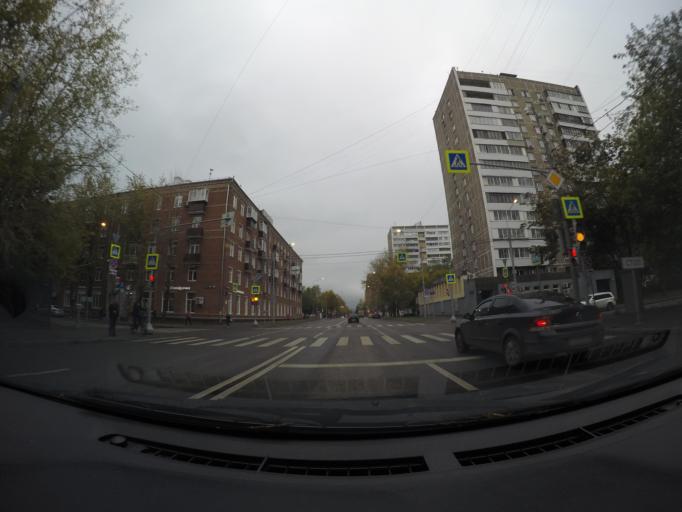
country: RU
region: Moskovskaya
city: Novogireyevo
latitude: 55.7565
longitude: 37.8039
